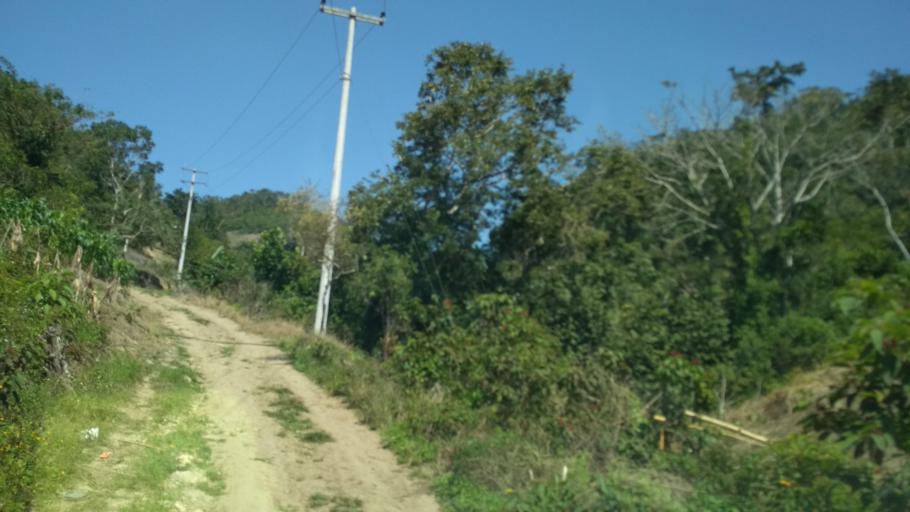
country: MX
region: Veracruz
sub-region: Papantla
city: Polutla
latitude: 20.4851
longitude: -97.2265
